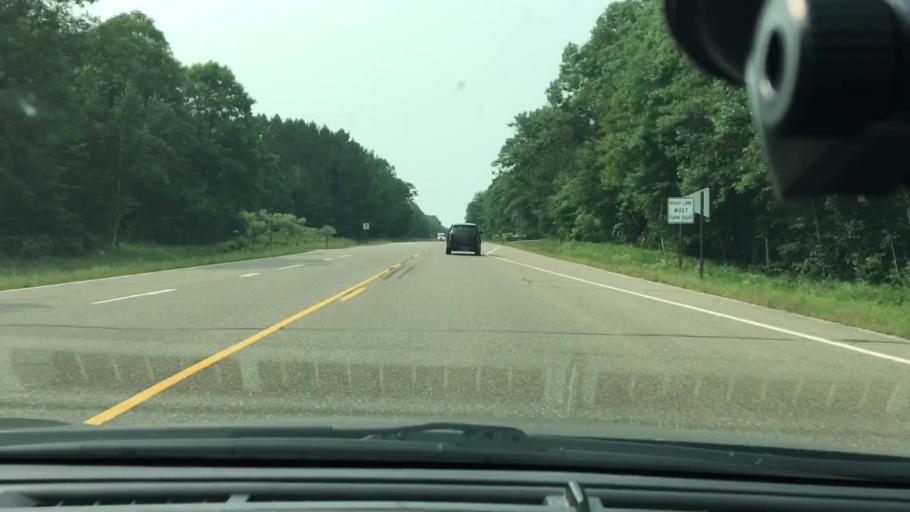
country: US
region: Minnesota
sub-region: Crow Wing County
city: Breezy Point
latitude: 46.5119
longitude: -94.1339
